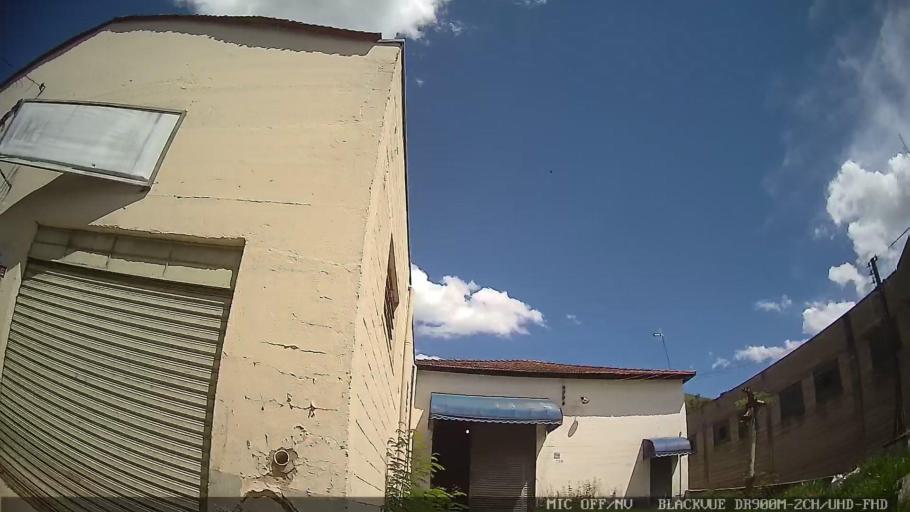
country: BR
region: Sao Paulo
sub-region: Pedreira
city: Pedreira
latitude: -22.7441
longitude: -46.9116
